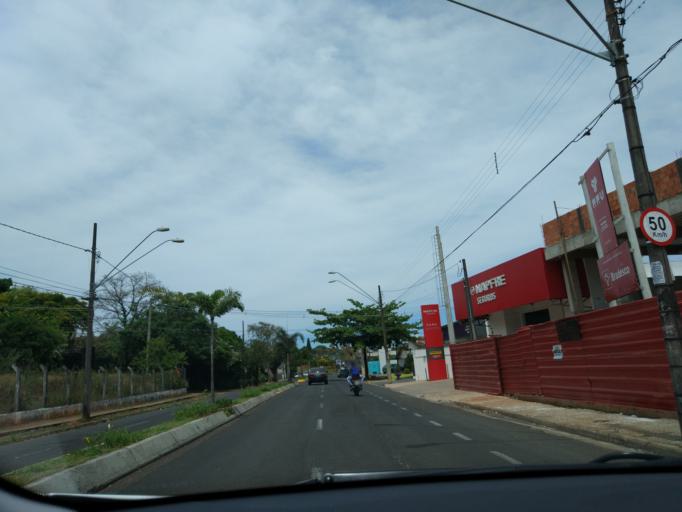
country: BR
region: Sao Paulo
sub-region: Botucatu
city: Botucatu
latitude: -22.8883
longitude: -48.4547
